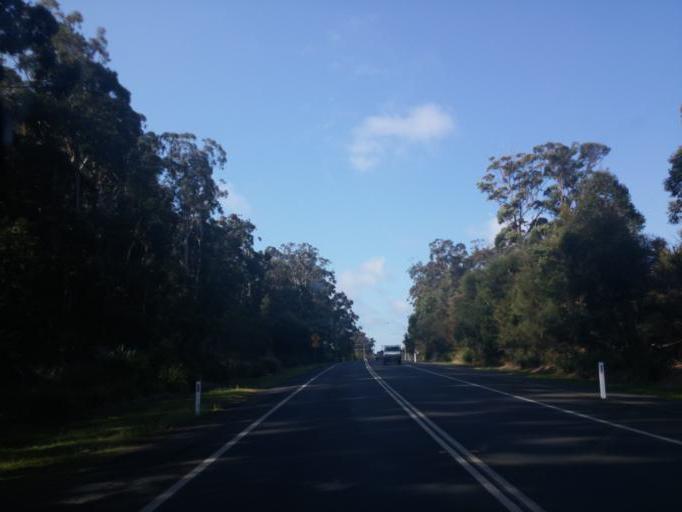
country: AU
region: New South Wales
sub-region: Coffs Harbour
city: Coffs Harbour
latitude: -30.2975
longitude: 153.1282
